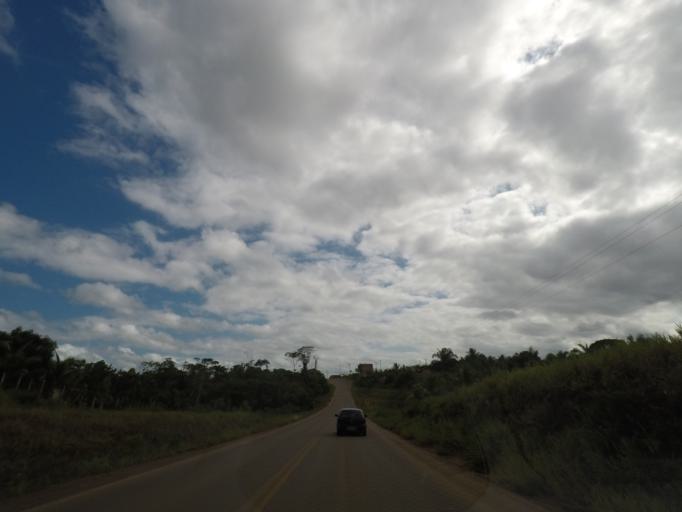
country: BR
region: Bahia
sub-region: Itacare
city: Itacare
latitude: -14.2104
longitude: -39.1008
